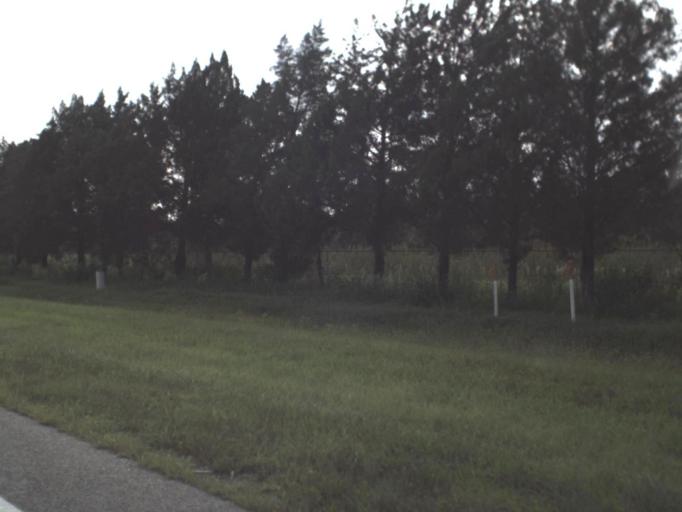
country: US
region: Florida
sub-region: Lee County
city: Alva
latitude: 26.7092
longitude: -81.6283
